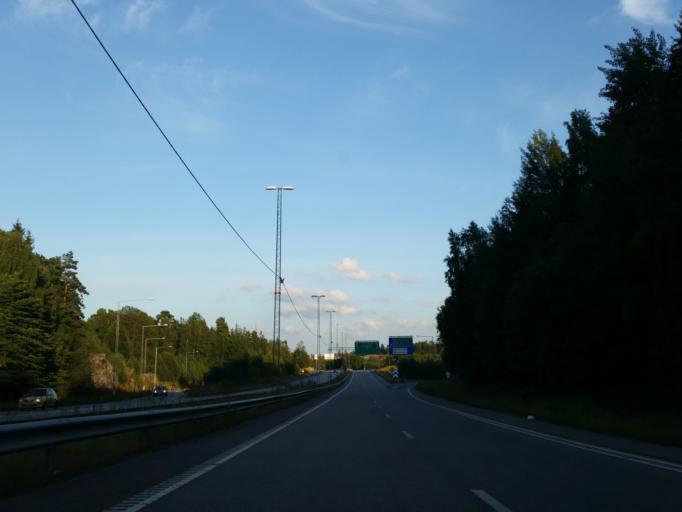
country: SE
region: Stockholm
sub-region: Sodertalje Kommun
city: Soedertaelje
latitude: 59.2028
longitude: 17.6523
